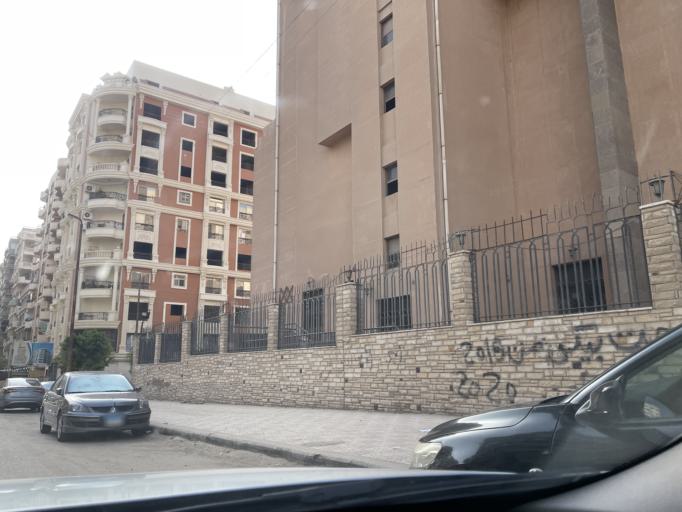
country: EG
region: Muhafazat al Qahirah
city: Cairo
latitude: 30.0672
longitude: 31.3524
